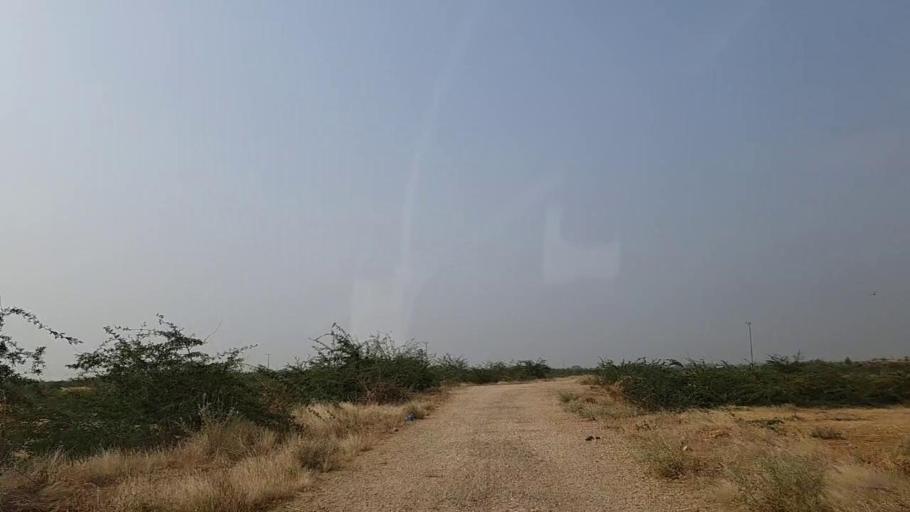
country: PK
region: Sindh
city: Thatta
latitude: 24.7210
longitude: 67.8305
